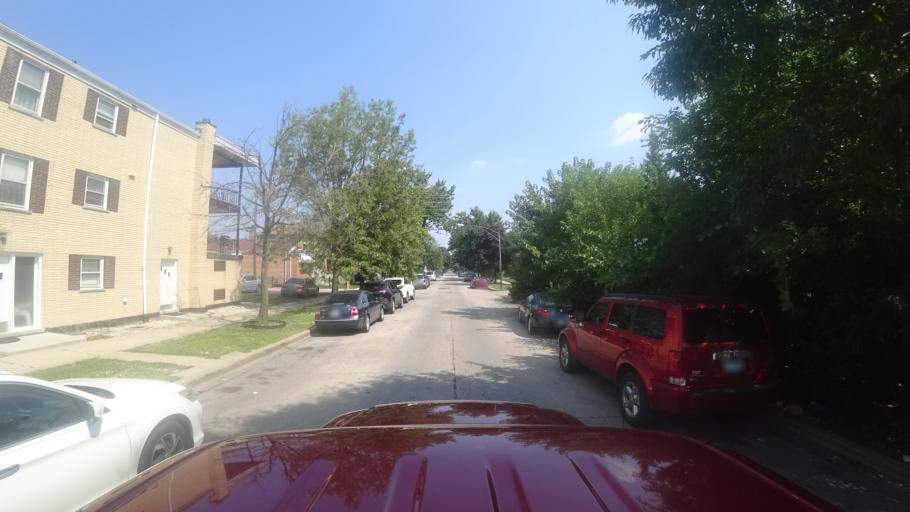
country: US
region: Illinois
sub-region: Cook County
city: Cicero
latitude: 41.7933
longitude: -87.7293
